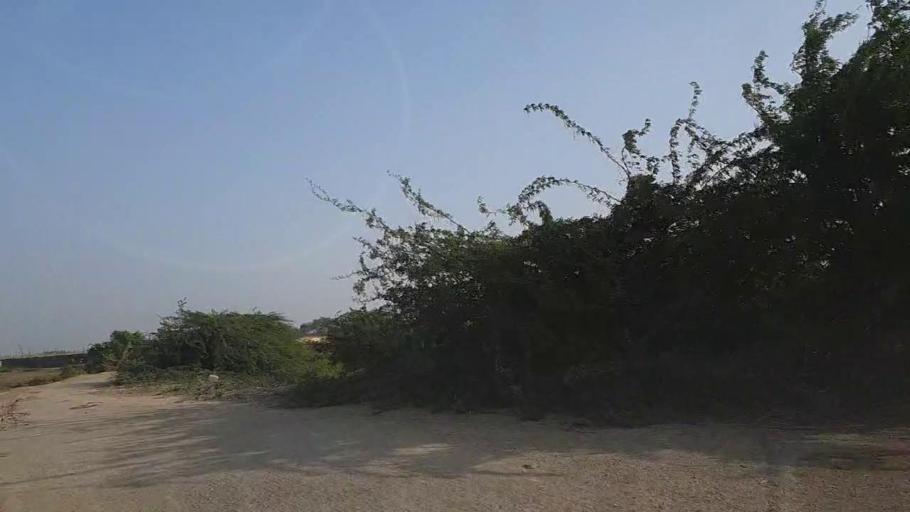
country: PK
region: Sindh
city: Keti Bandar
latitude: 24.1664
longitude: 67.6270
